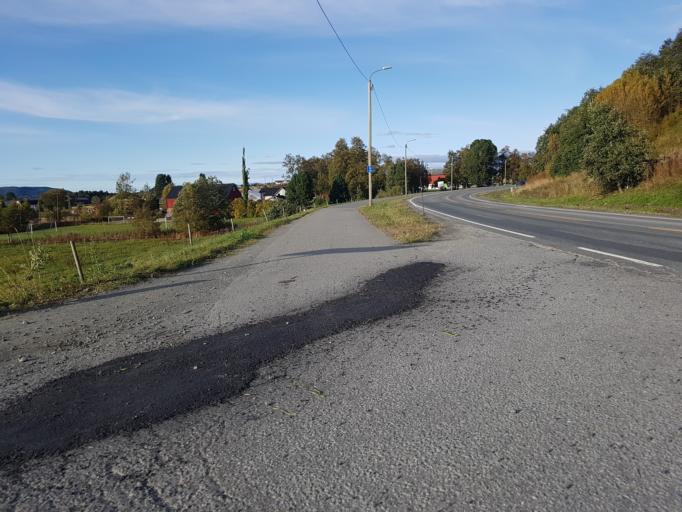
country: NO
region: Sor-Trondelag
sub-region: Trondheim
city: Trondheim
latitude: 63.3743
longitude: 10.4299
